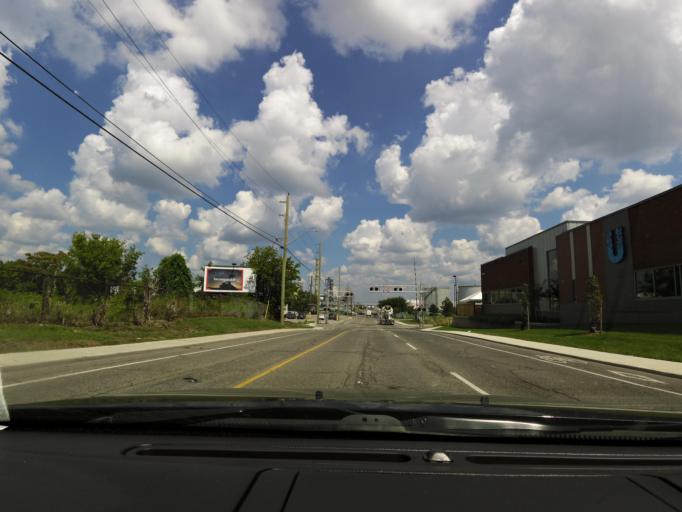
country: CA
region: Ontario
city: Hamilton
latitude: 43.2678
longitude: -79.8505
